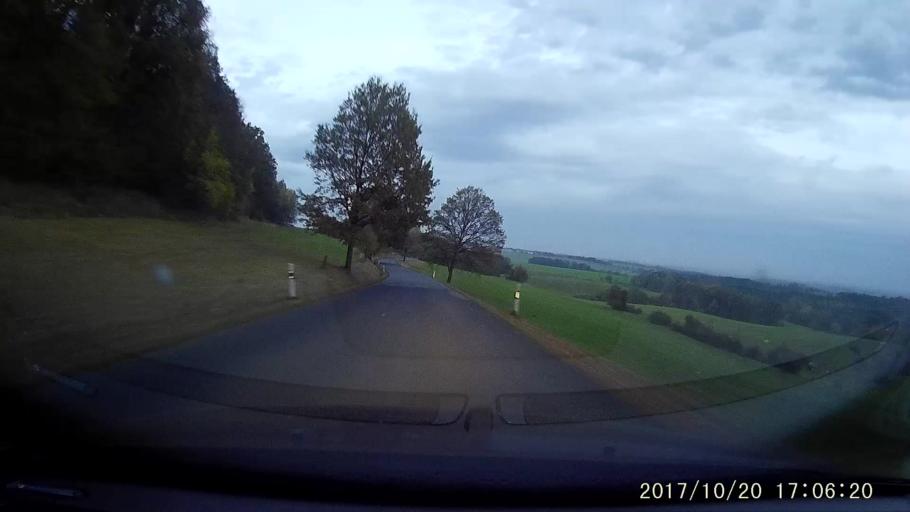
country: DE
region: Saxony
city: Schonau-Berzdorf
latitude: 51.0977
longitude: 14.9159
